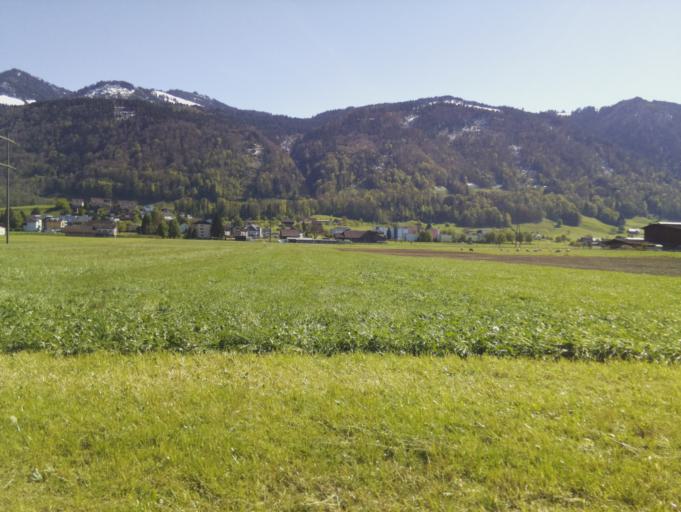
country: CH
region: Schwyz
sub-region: Bezirk March
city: Schubelbach
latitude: 47.1802
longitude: 8.9369
